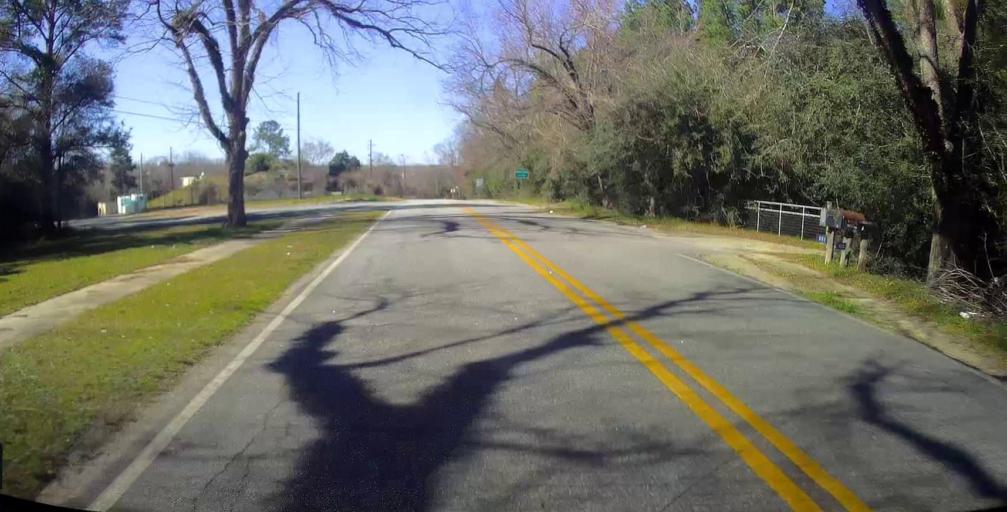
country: US
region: Georgia
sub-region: Macon County
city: Montezuma
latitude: 32.2823
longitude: -84.0300
